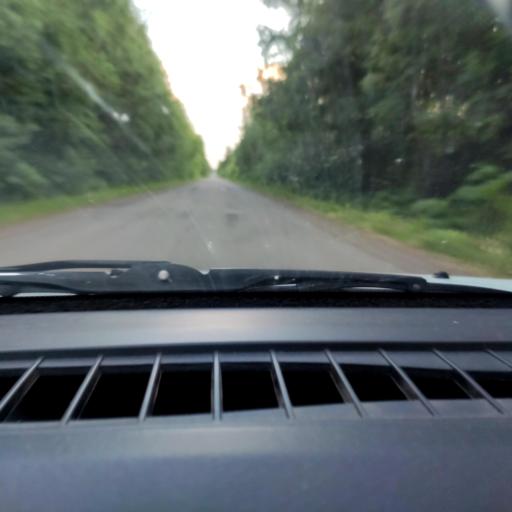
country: RU
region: Perm
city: Orda
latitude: 57.2622
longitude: 56.5336
